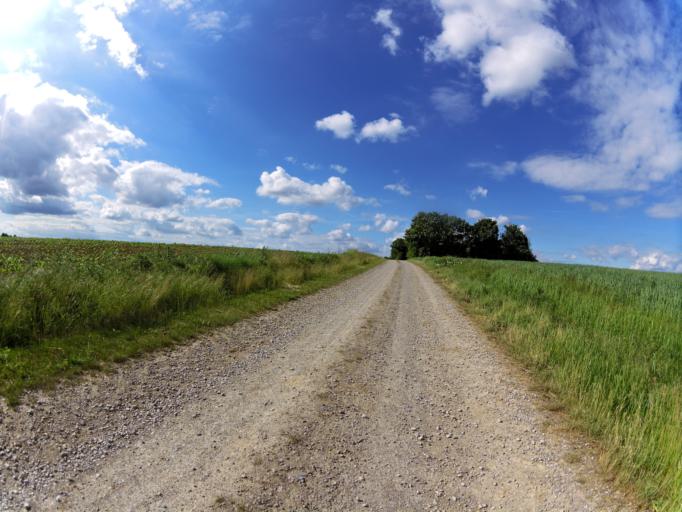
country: DE
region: Bavaria
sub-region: Regierungsbezirk Unterfranken
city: Gaukonigshofen
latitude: 49.6595
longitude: 10.0246
